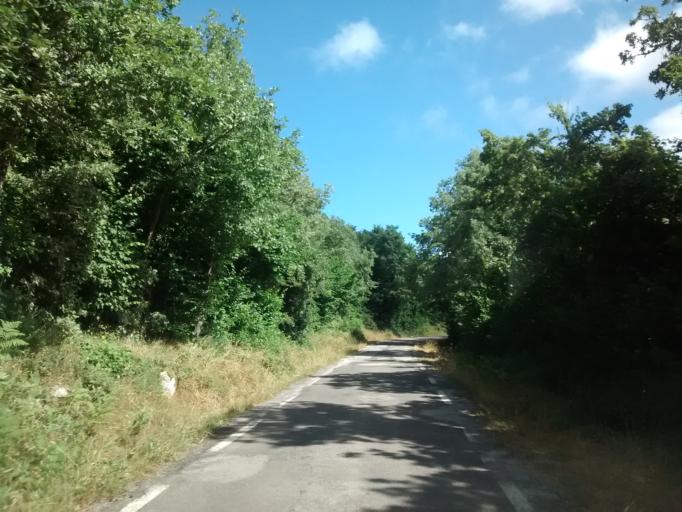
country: ES
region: Castille and Leon
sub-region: Provincia de Palencia
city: Berzosilla
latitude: 42.8765
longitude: -4.0530
